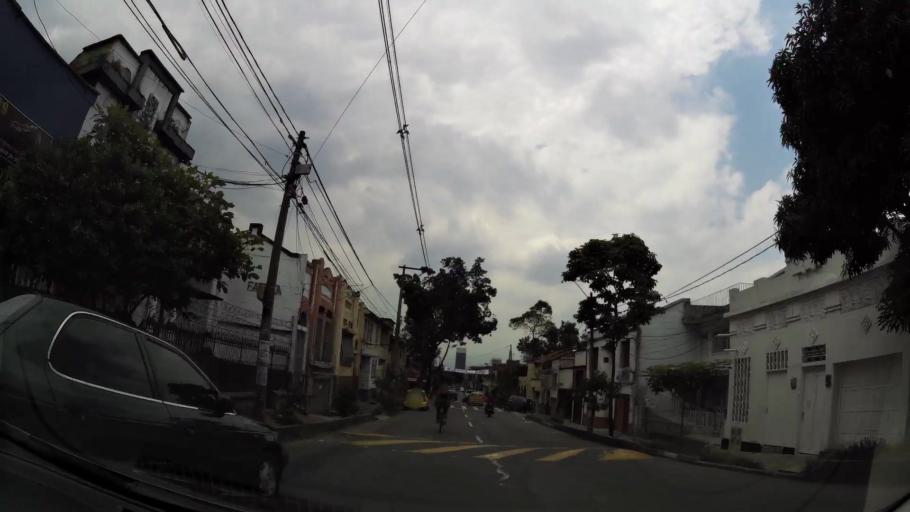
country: CO
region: Antioquia
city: Medellin
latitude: 6.2612
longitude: -75.5590
